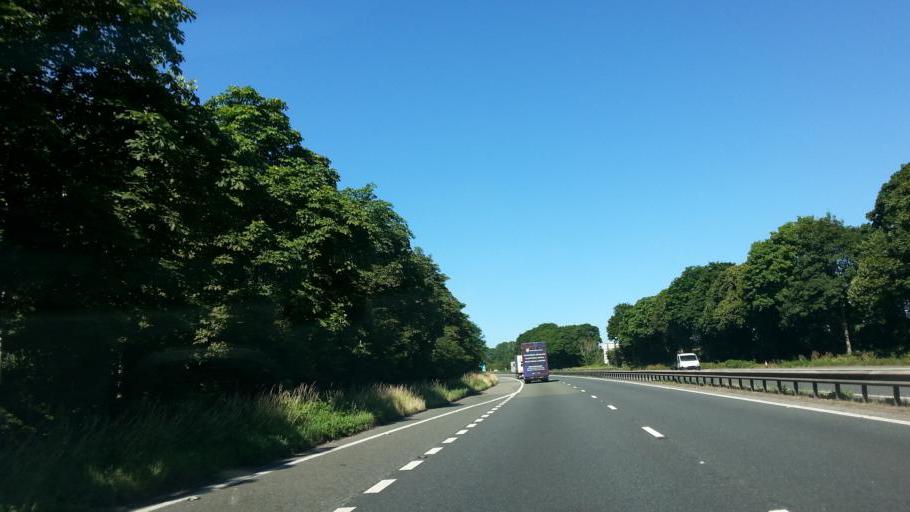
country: GB
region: England
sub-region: Herefordshire
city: Donnington
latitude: 51.9973
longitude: -2.3644
